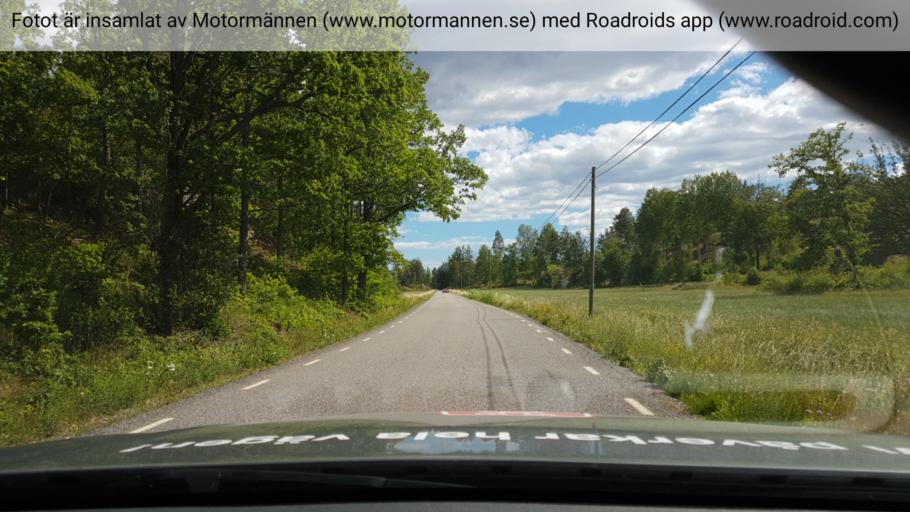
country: SE
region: Kalmar
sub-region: Vasterviks Kommun
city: Forserum
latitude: 57.9844
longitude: 16.6073
